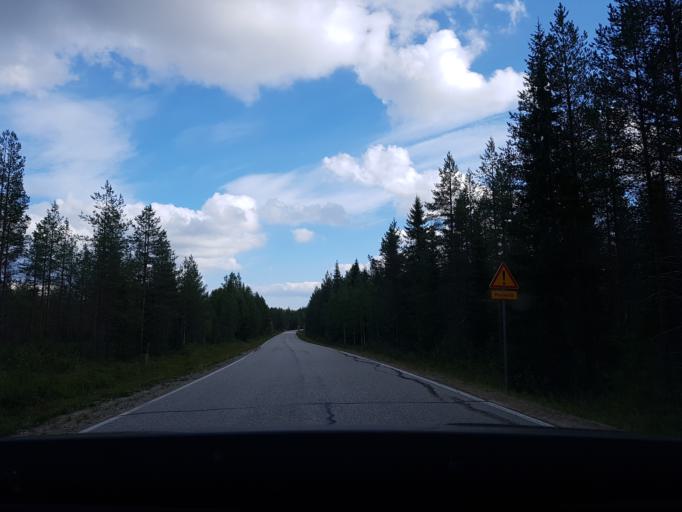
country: FI
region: Kainuu
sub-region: Kehys-Kainuu
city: Kuhmo
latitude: 64.6291
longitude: 29.6922
